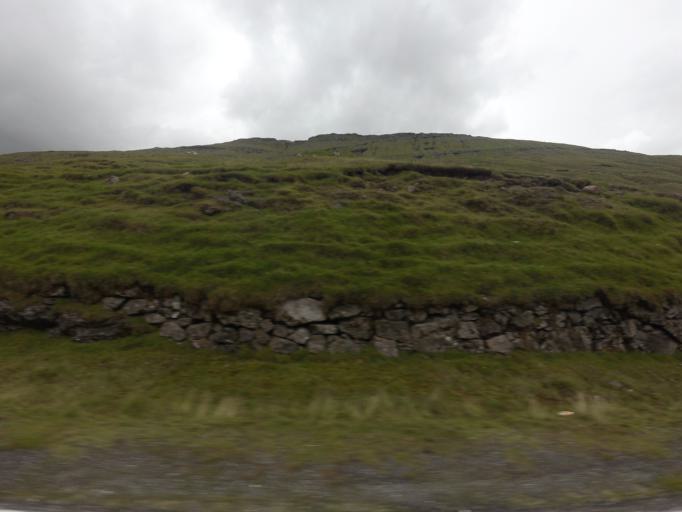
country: FO
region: Streymoy
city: Kollafjordhur
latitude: 62.1217
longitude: -6.9895
